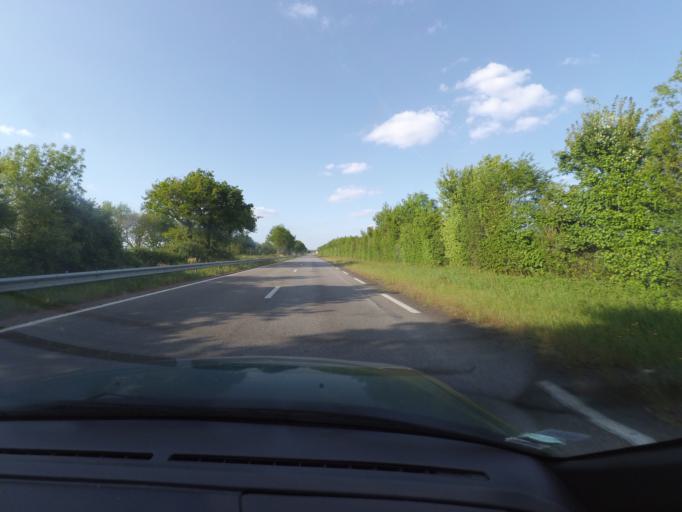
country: FR
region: Pays de la Loire
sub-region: Departement de la Vendee
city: Saligny
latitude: 46.8508
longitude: -1.4124
